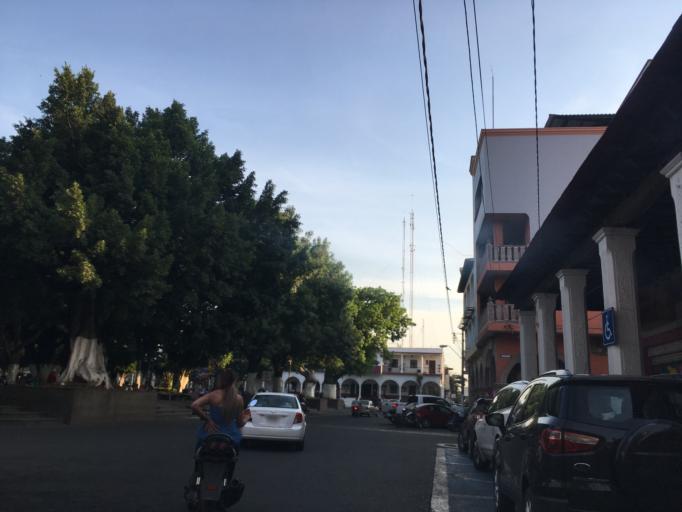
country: MX
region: Michoacan
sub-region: Los Reyes
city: La Higuerita (Colonia San Rafael)
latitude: 19.5900
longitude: -102.4743
